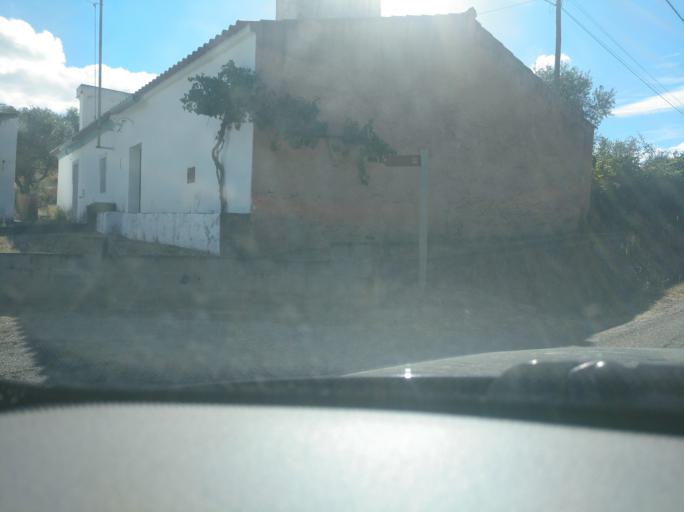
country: ES
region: Extremadura
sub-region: Provincia de Badajoz
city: La Codosera
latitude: 39.1539
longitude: -7.1655
